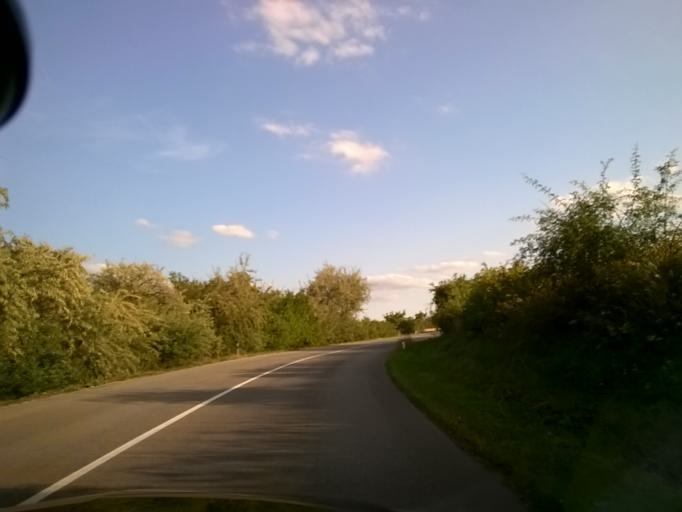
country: SK
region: Nitriansky
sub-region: Okres Nitra
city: Nitra
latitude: 48.3087
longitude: 17.9243
